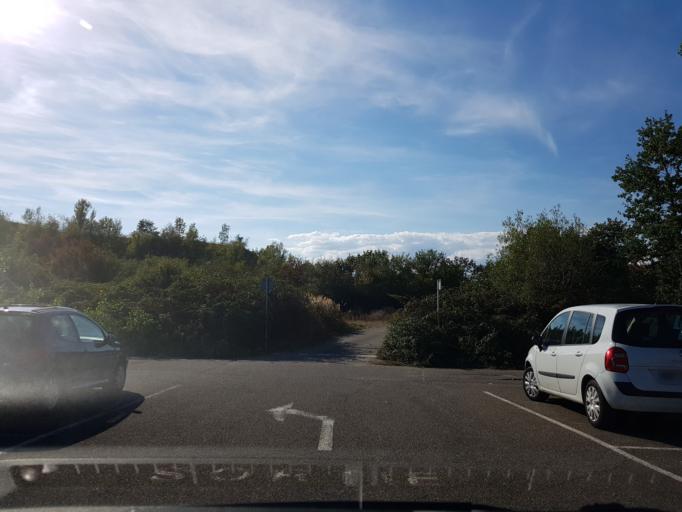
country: FR
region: Alsace
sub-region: Departement du Haut-Rhin
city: Pulversheim
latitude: 47.8526
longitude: 7.2845
